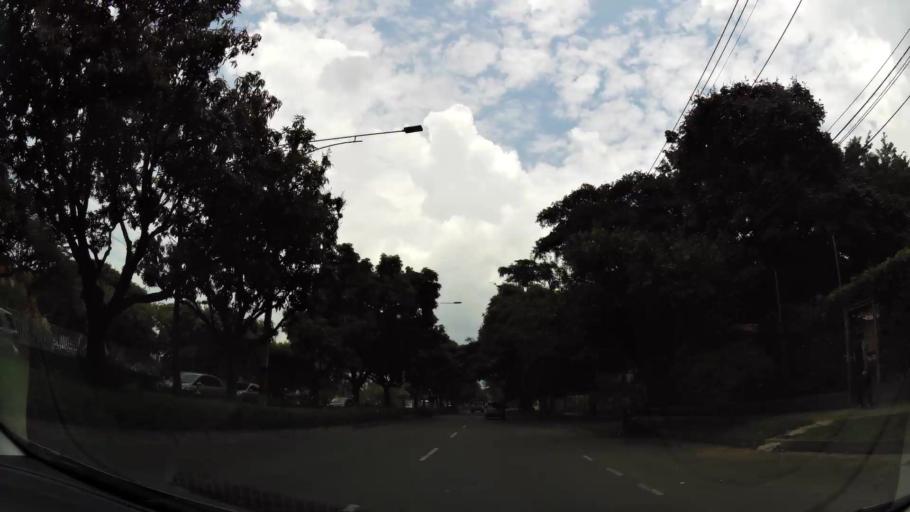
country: CO
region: Antioquia
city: Envigado
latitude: 6.1672
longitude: -75.5984
